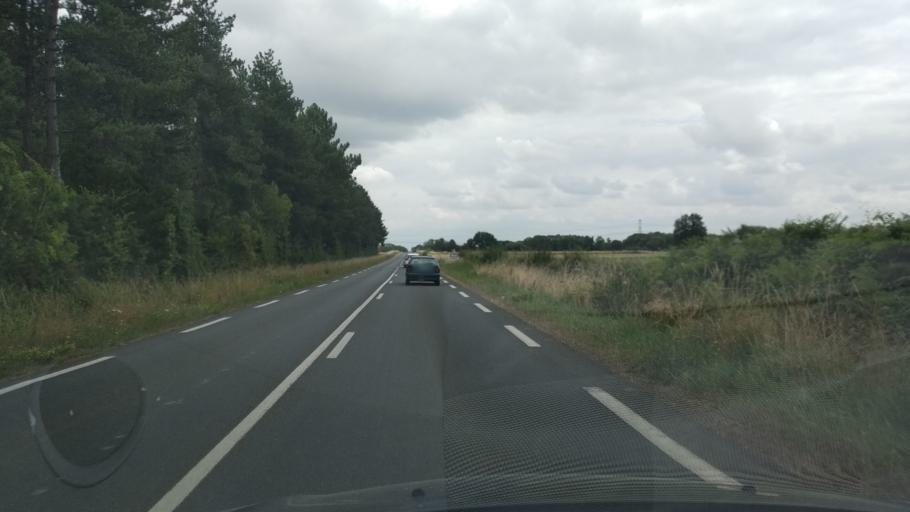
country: FR
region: Poitou-Charentes
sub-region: Departement de la Vienne
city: Saint-Maurice-la-Clouere
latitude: 46.4050
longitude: 0.3918
